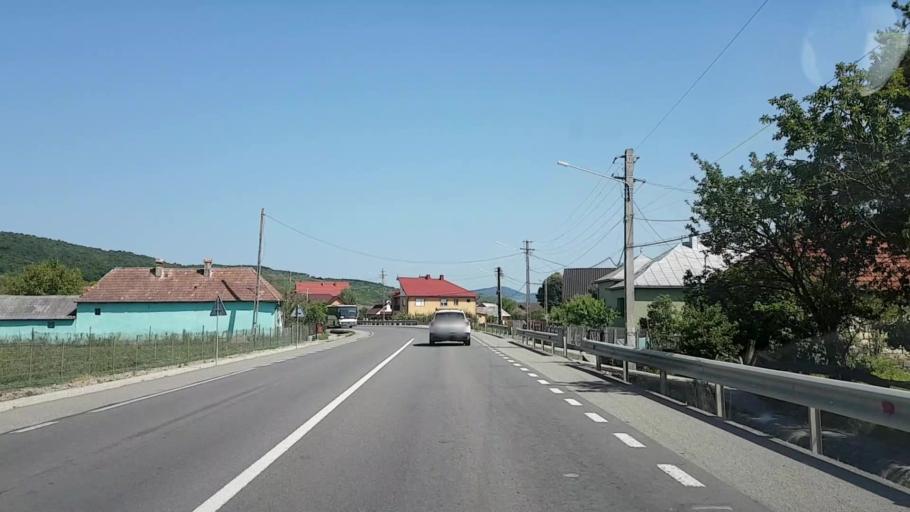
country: RO
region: Bistrita-Nasaud
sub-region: Comuna Sintereag
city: Sintereag
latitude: 47.1789
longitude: 24.2946
